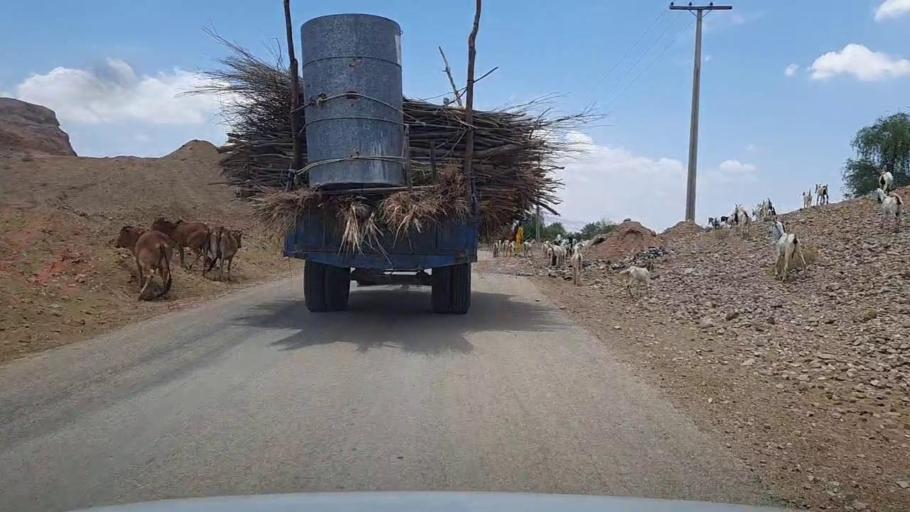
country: PK
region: Sindh
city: Bhan
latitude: 26.3158
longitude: 67.5871
